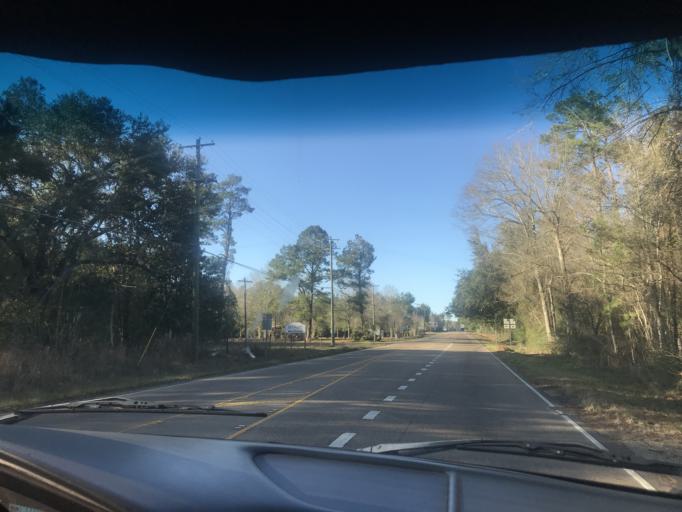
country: US
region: Louisiana
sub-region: Saint Tammany Parish
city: Covington
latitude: 30.5582
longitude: -90.1494
